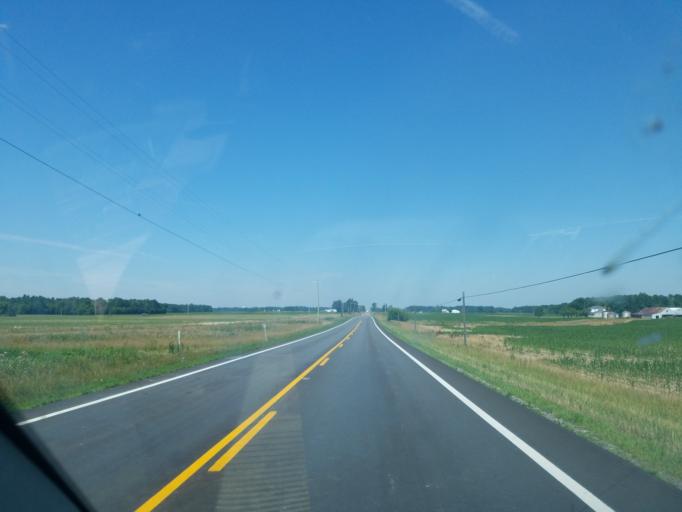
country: US
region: Ohio
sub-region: Shelby County
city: Botkins
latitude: 40.4389
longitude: -84.1304
